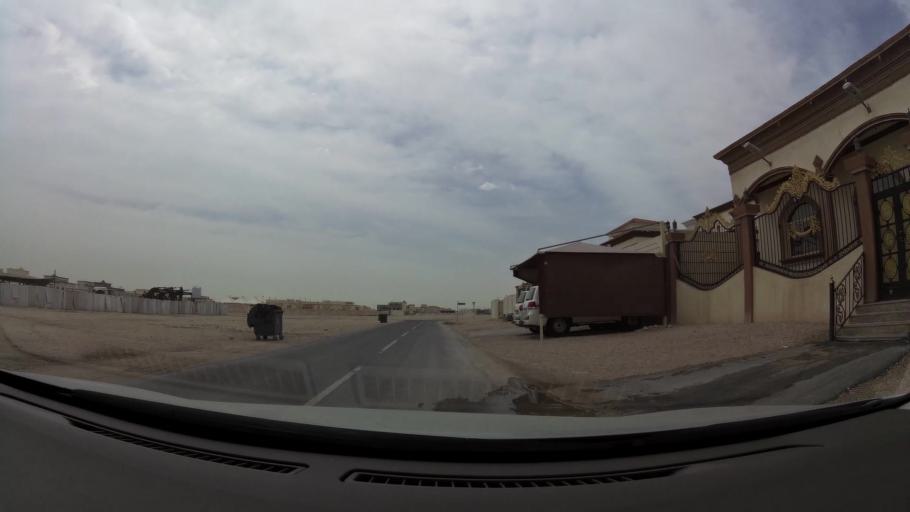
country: QA
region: Baladiyat ar Rayyan
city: Ar Rayyan
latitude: 25.2150
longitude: 51.4514
